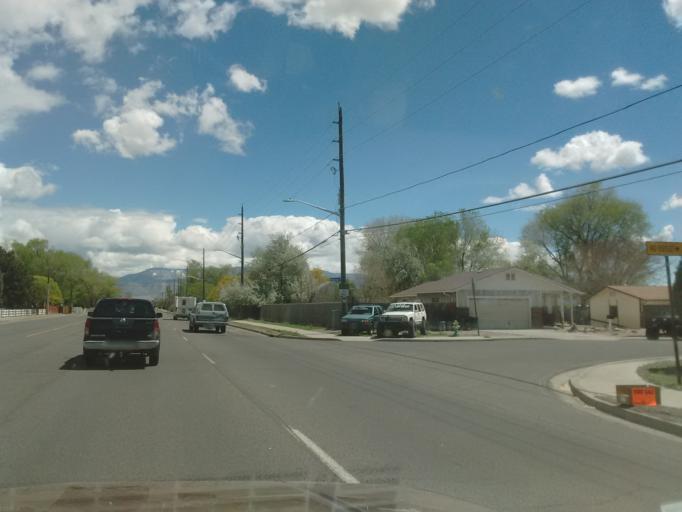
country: US
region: Colorado
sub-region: Mesa County
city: Fruitvale
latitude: 39.0918
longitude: -108.5113
